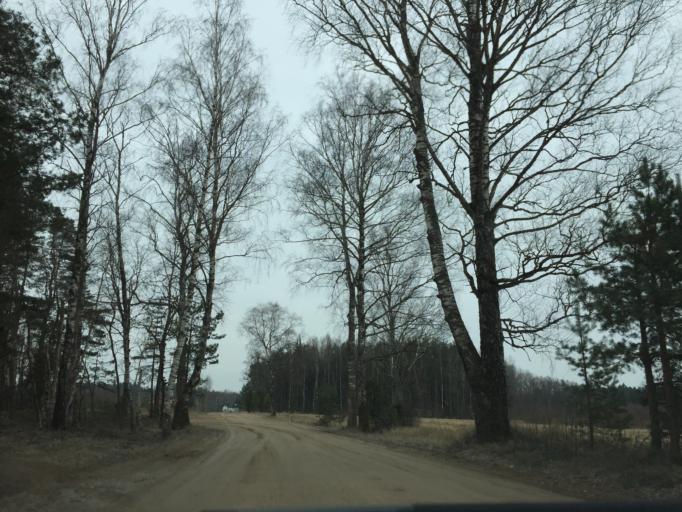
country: LV
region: Kekava
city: Kekava
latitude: 56.7997
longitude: 24.1643
